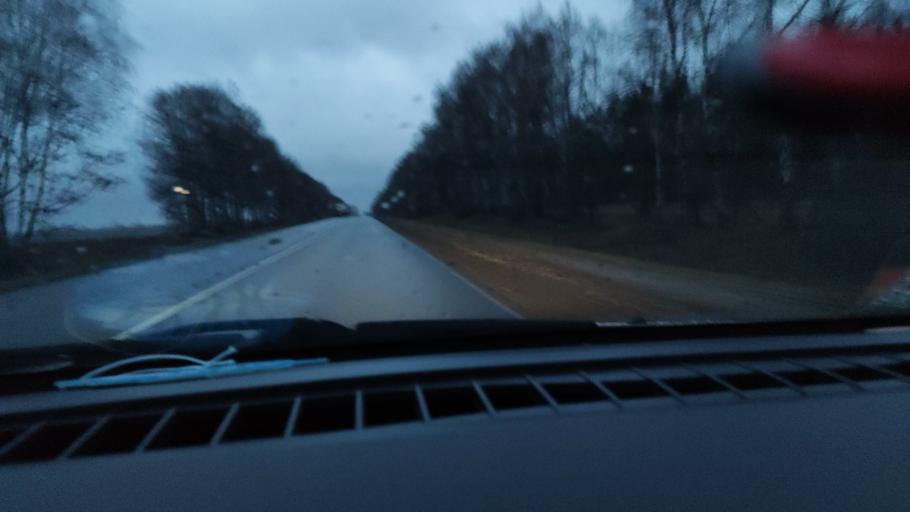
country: RU
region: Udmurtiya
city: Mozhga
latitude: 56.3123
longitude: 52.3320
